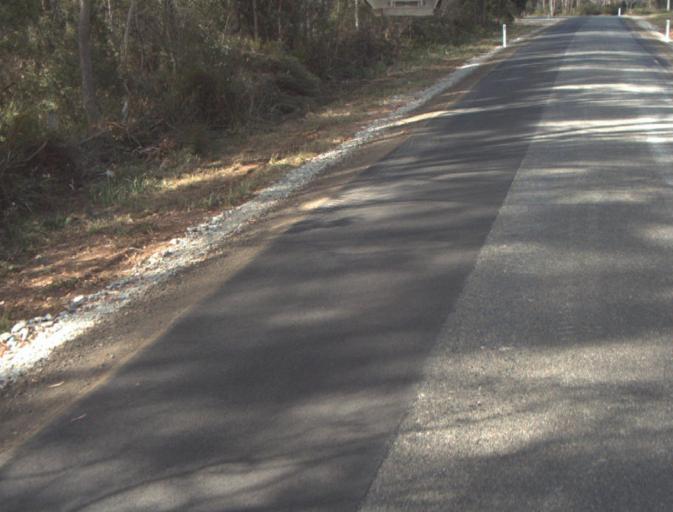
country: AU
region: Tasmania
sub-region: Launceston
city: Mayfield
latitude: -41.3108
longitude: 147.1985
